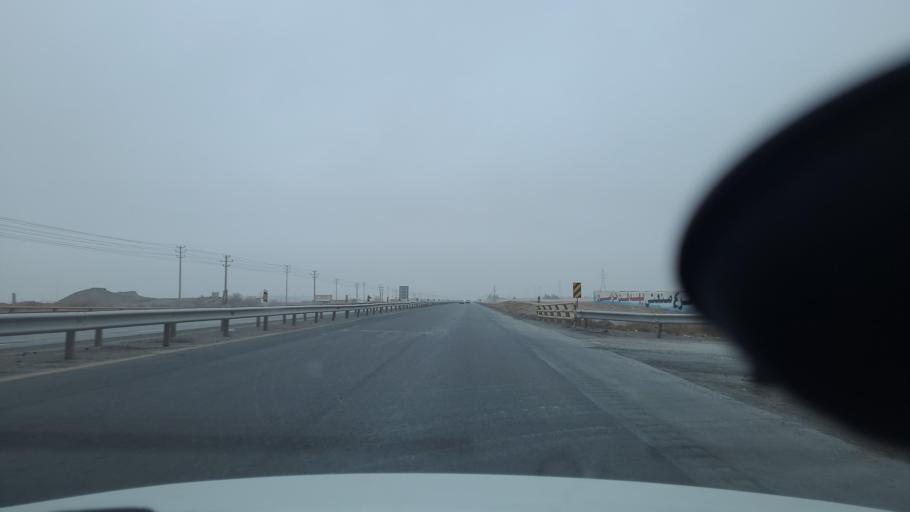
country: IR
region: Razavi Khorasan
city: Fariman
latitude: 35.9324
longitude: 59.7519
